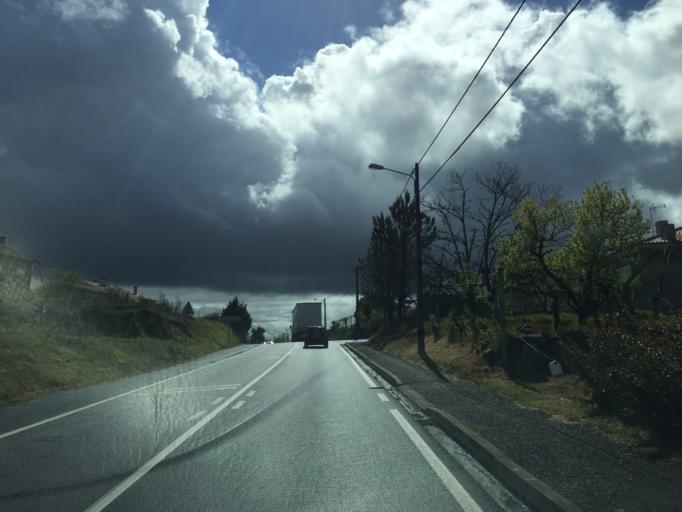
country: PT
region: Coimbra
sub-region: Oliveira do Hospital
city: Oliveira do Hospital
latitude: 40.3321
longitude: -7.8680
